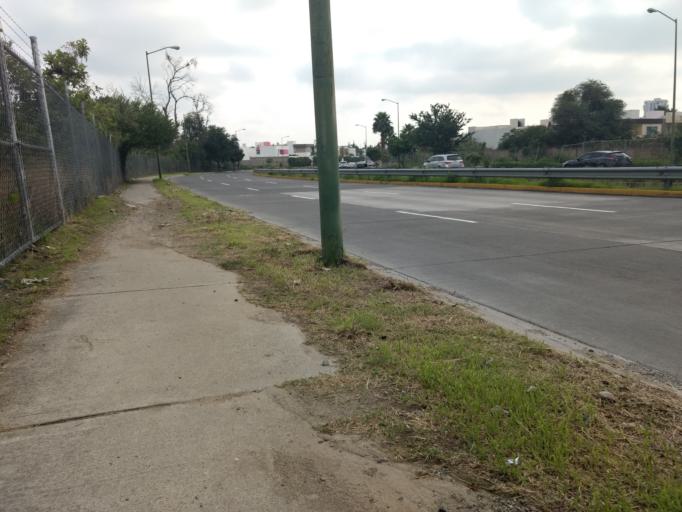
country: MX
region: Jalisco
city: Guadalajara
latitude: 20.6600
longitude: -103.4392
